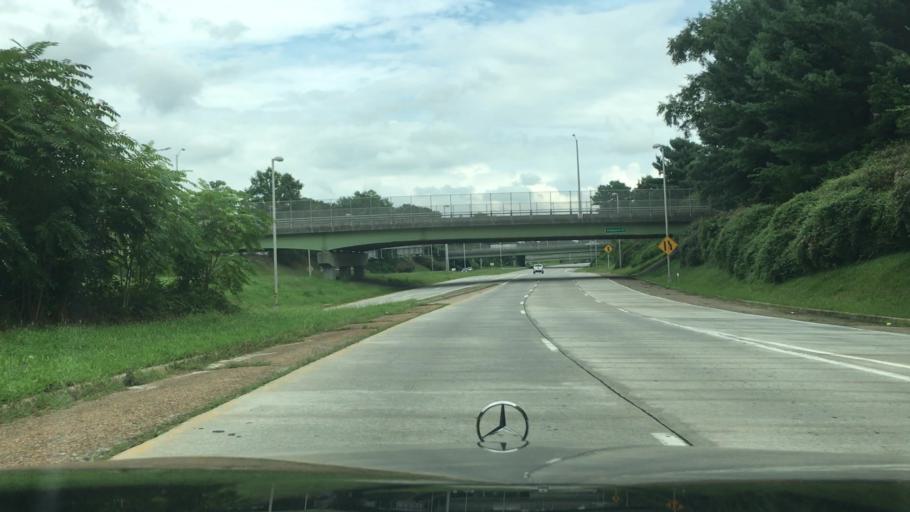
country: US
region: Virginia
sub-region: City of Richmond
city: Richmond
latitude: 37.5497
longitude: -77.4813
